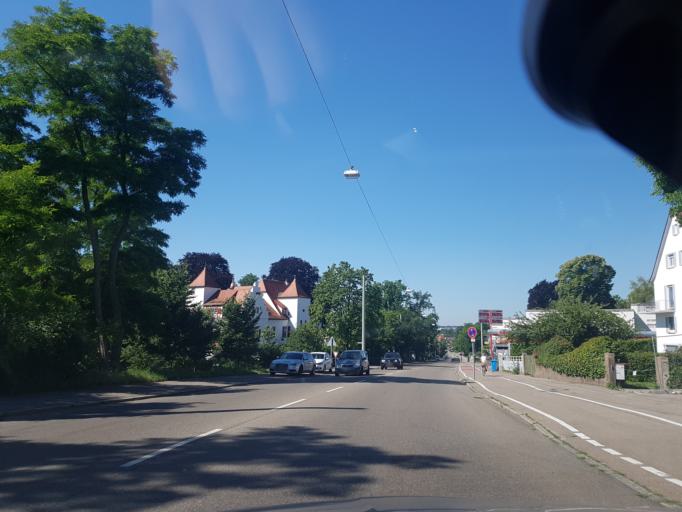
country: DE
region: Bavaria
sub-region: Swabia
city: Neu-Ulm
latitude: 48.4121
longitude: 10.0066
